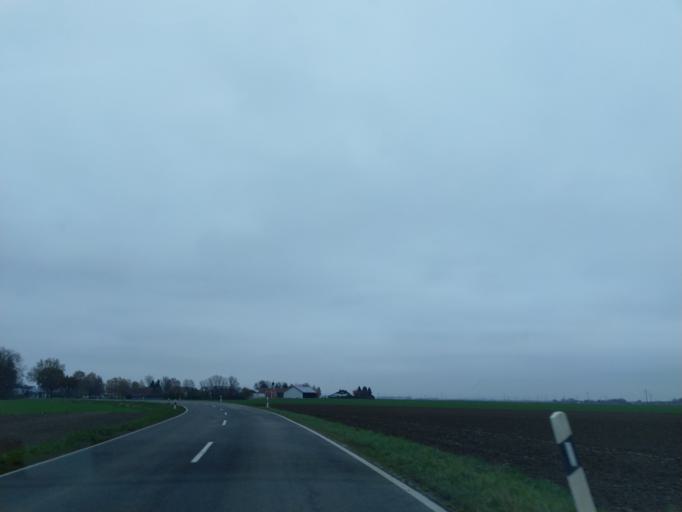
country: DE
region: Bavaria
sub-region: Lower Bavaria
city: Otzing
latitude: 48.7631
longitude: 12.7799
